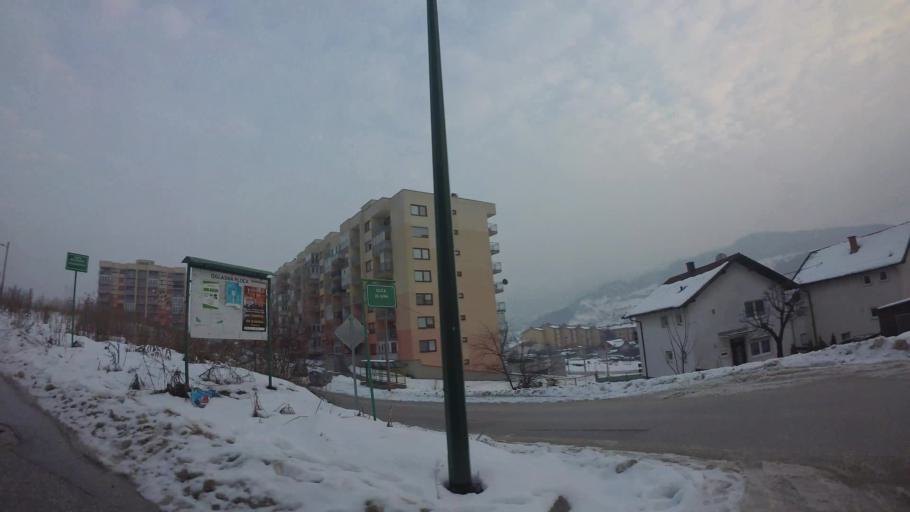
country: BA
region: Federation of Bosnia and Herzegovina
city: Vogosca
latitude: 43.9034
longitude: 18.3493
